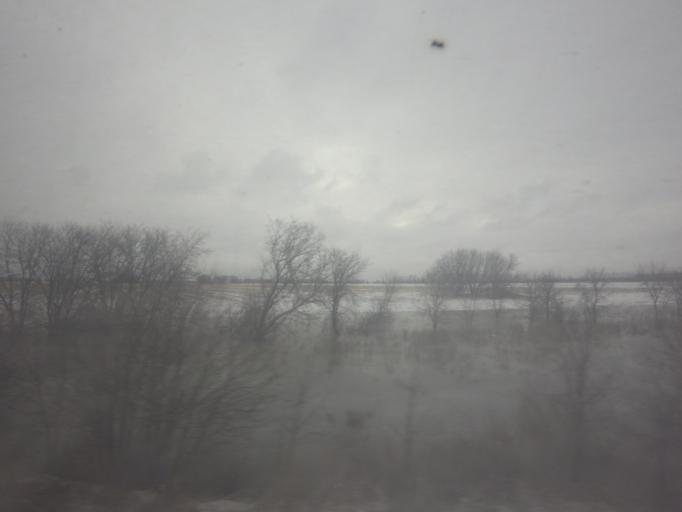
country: CA
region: Ontario
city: Bells Corners
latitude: 45.2119
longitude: -75.8080
